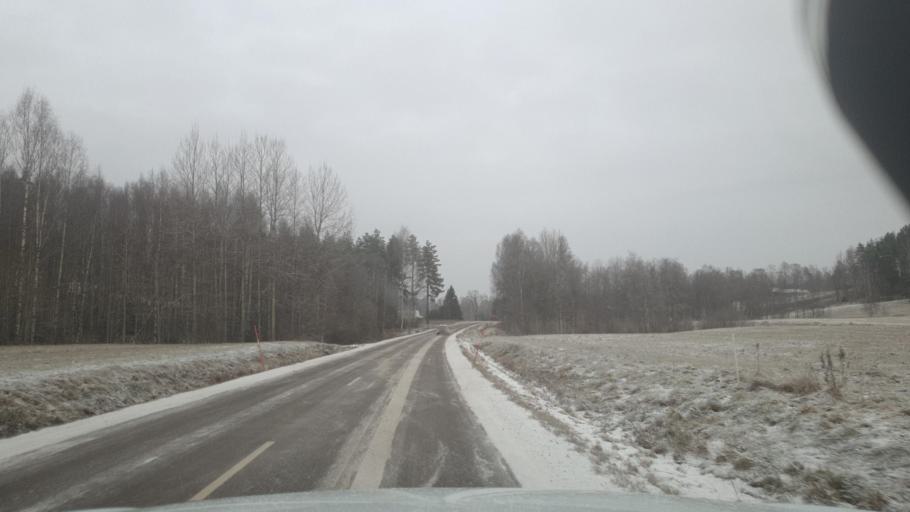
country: SE
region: Vaermland
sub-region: Arvika Kommun
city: Arvika
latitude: 59.6381
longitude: 12.8861
